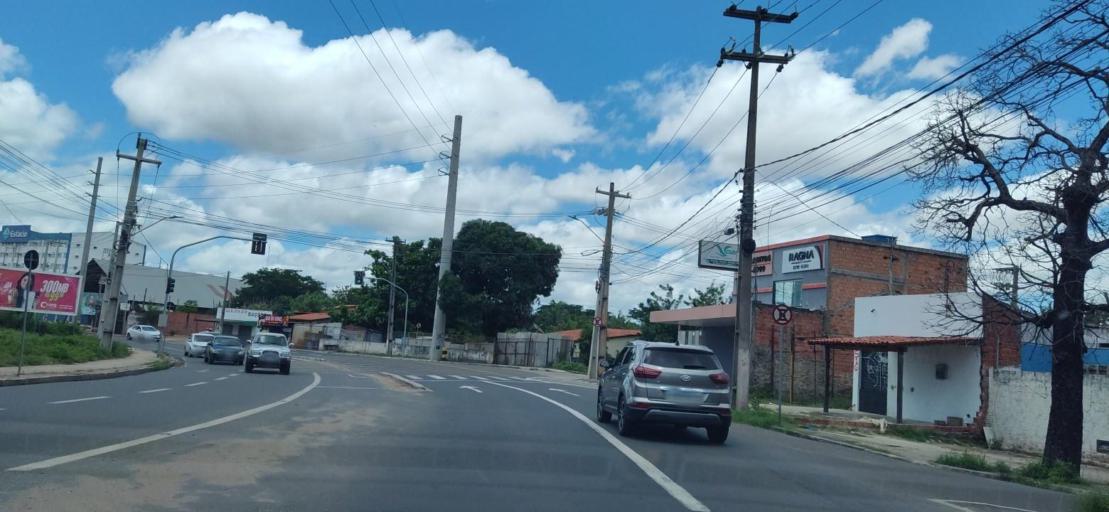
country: BR
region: Piaui
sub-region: Teresina
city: Teresina
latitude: -5.0862
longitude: -42.7658
